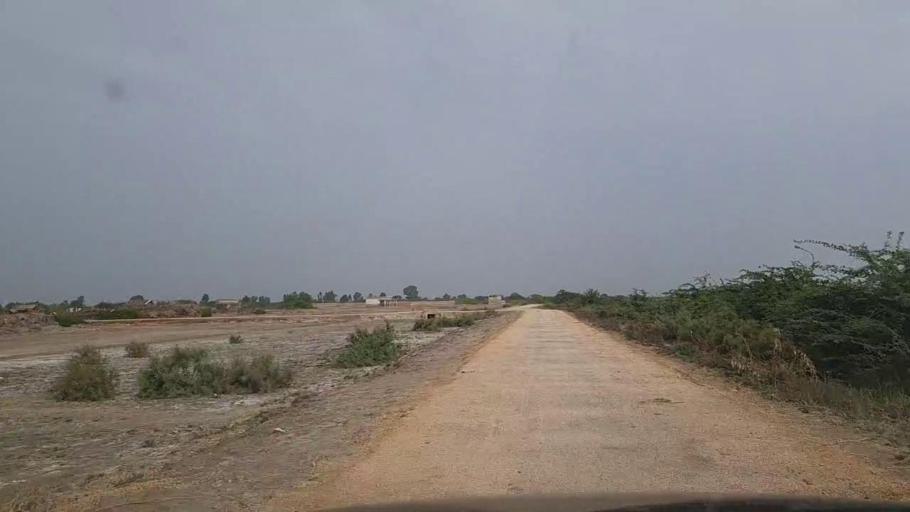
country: PK
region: Sindh
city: Thatta
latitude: 24.7499
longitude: 67.8267
